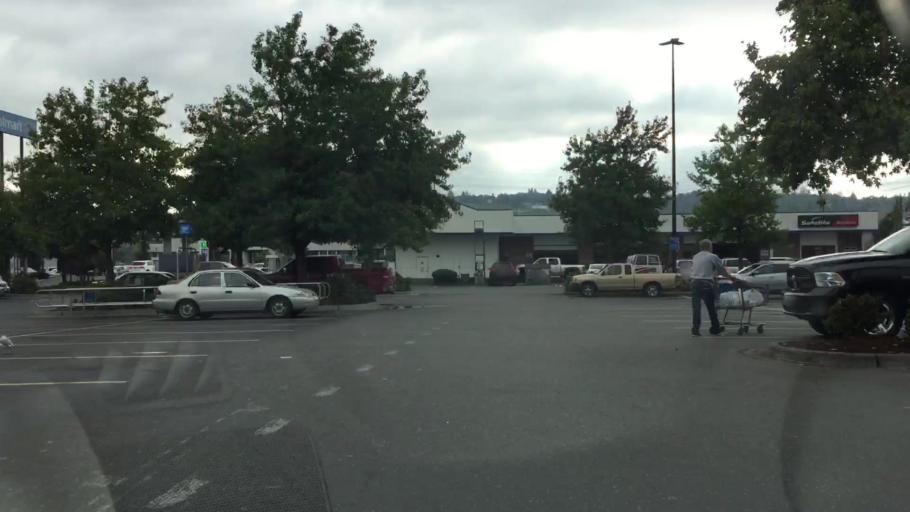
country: US
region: Washington
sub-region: King County
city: Renton
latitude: 47.4717
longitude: -122.2194
